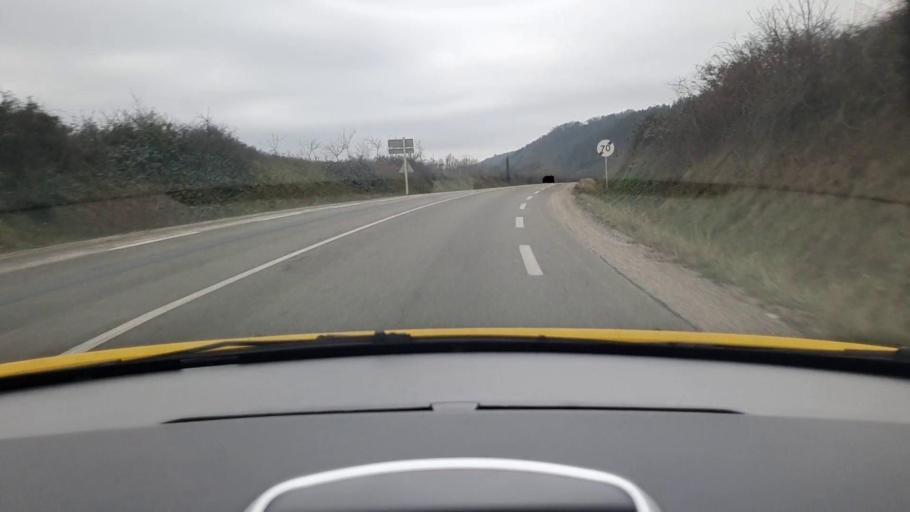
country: FR
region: Languedoc-Roussillon
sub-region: Departement du Gard
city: Saint-Ambroix
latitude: 44.2712
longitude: 4.1832
